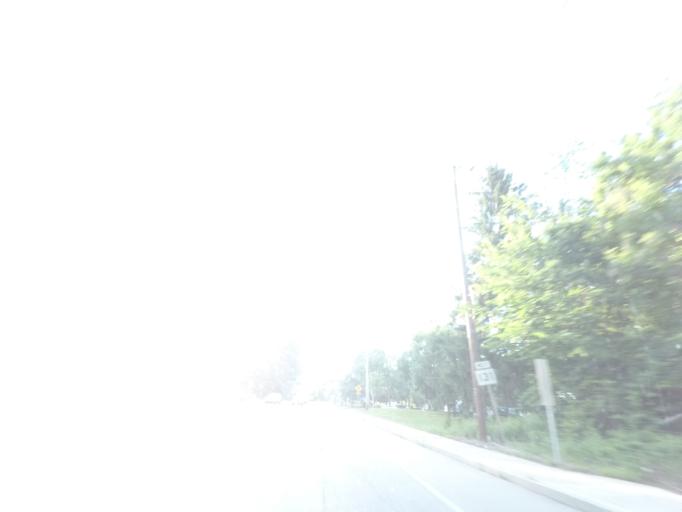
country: US
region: Massachusetts
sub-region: Worcester County
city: Sturbridge
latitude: 42.1100
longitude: -72.0828
